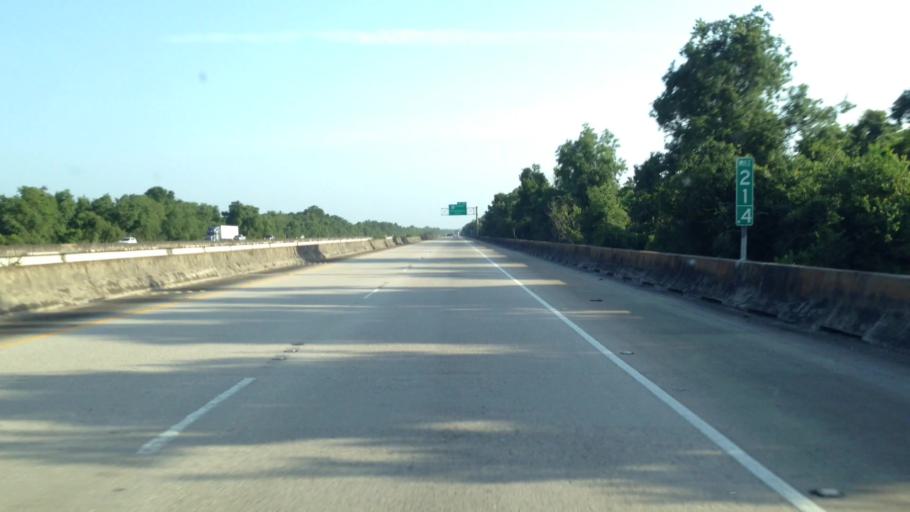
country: US
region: Louisiana
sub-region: Tangipahoa Parish
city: Ponchatoula
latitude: 30.3806
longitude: -90.4250
